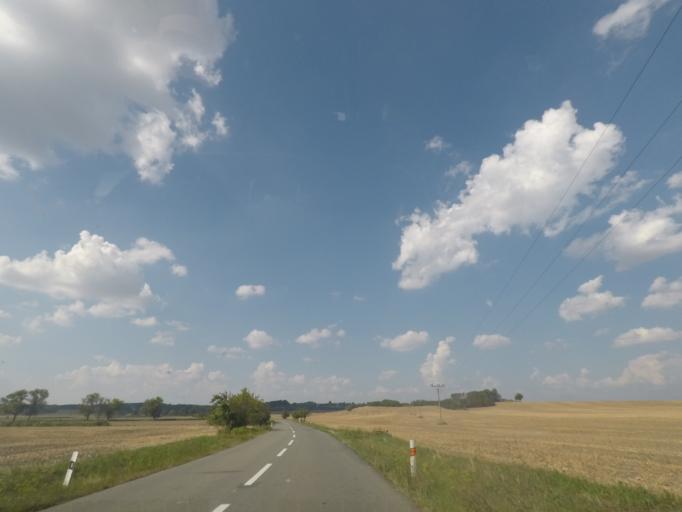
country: CZ
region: Kralovehradecky
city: Trebechovice pod Orebem
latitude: 50.2083
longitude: 15.9897
